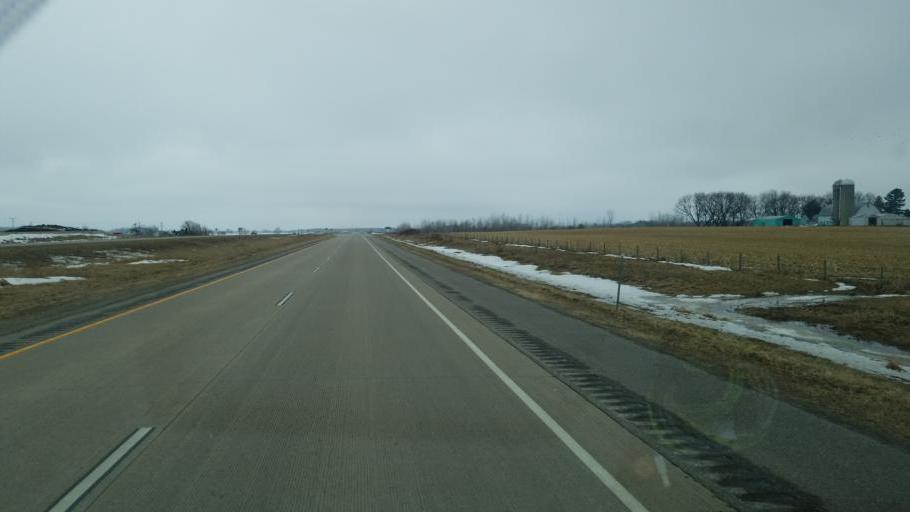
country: US
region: Wisconsin
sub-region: Wood County
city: Marshfield
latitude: 44.6202
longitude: -89.9996
